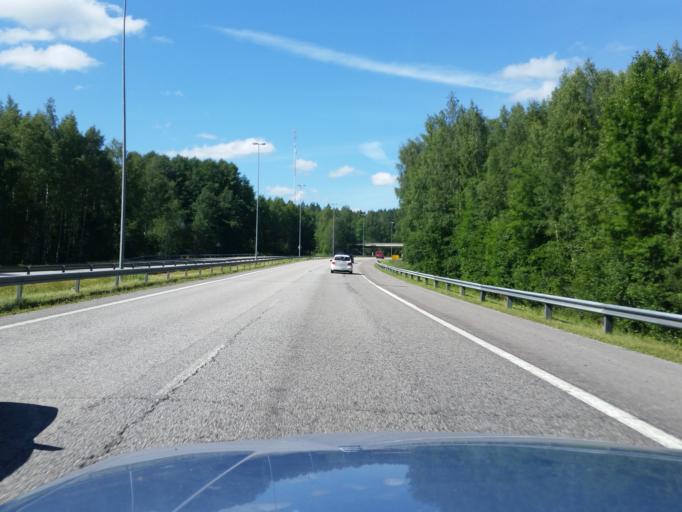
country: FI
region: Uusimaa
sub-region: Helsinki
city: Vihti
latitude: 60.2924
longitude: 24.3358
